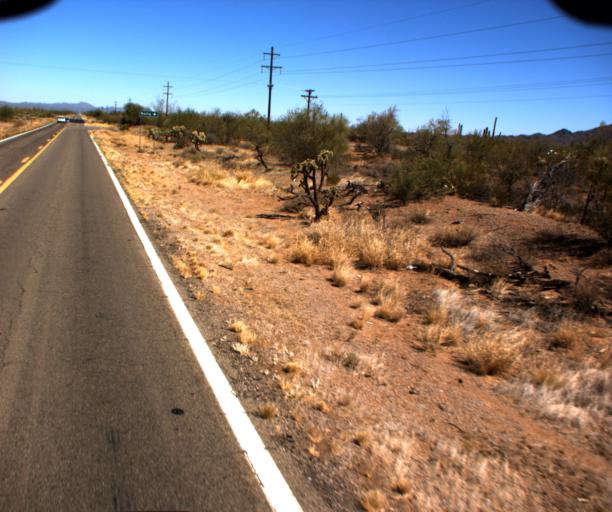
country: US
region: Arizona
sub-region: Pima County
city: Sells
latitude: 32.0130
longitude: -111.9956
